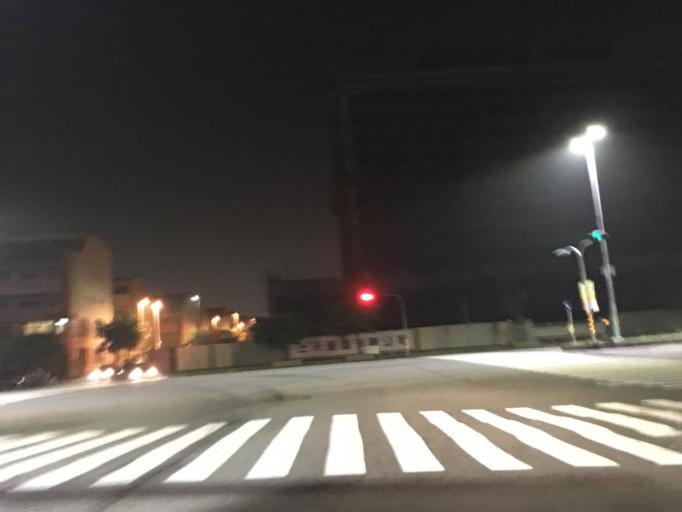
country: TW
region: Taiwan
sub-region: Chiayi
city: Taibao
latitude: 23.4694
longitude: 120.2956
